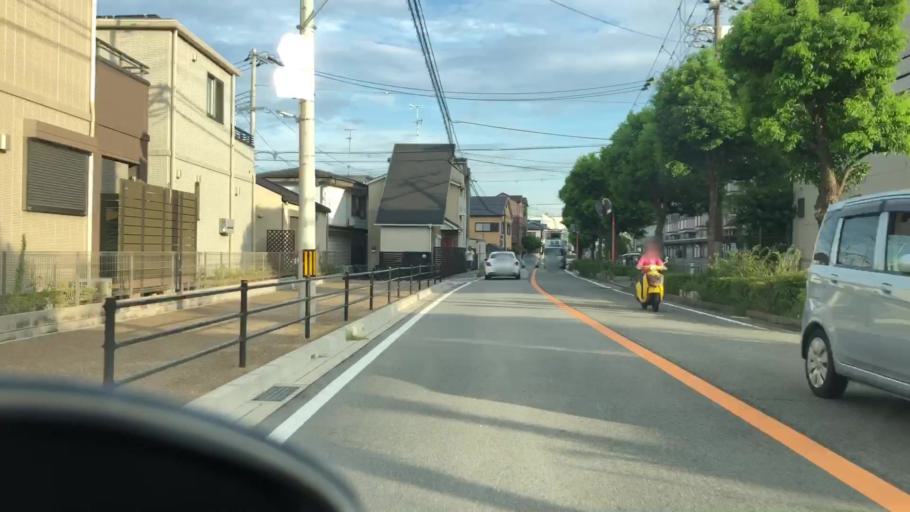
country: JP
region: Hyogo
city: Takarazuka
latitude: 34.7949
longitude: 135.3651
